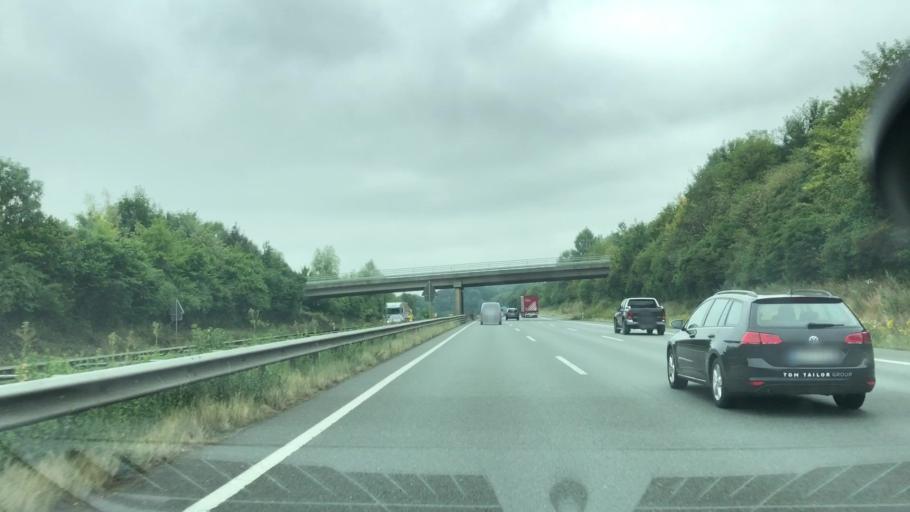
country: DE
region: North Rhine-Westphalia
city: Bad Oeynhausen
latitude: 52.1747
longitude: 8.8178
